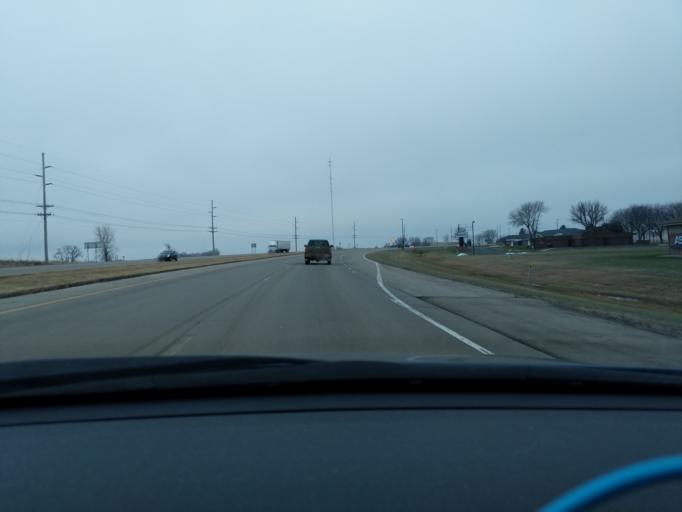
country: US
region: Minnesota
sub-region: Lyon County
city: Marshall
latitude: 44.4485
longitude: -95.7562
